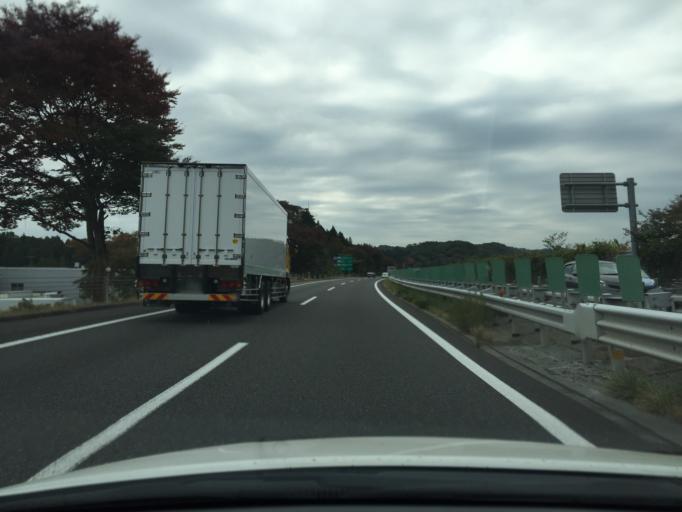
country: JP
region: Fukushima
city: Sukagawa
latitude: 37.1859
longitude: 140.2907
